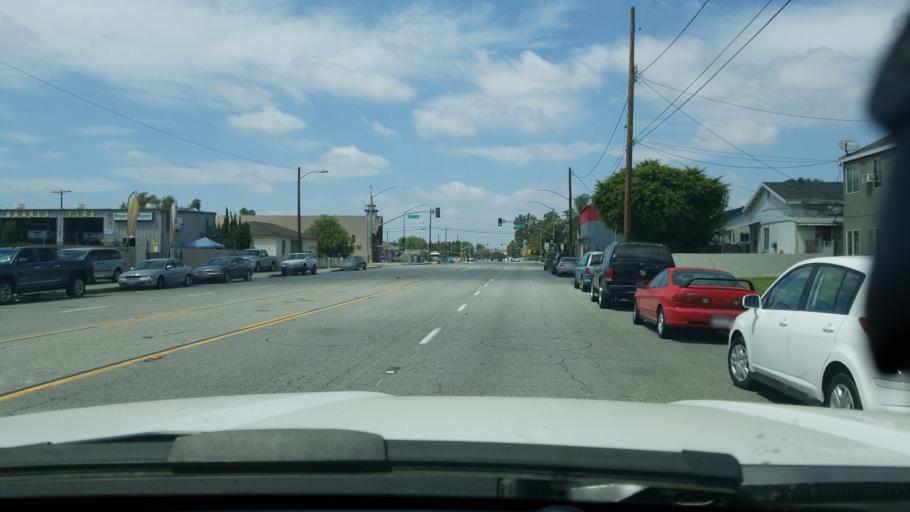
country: US
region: California
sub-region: Los Angeles County
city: South Whittier
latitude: 33.9271
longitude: -118.0484
